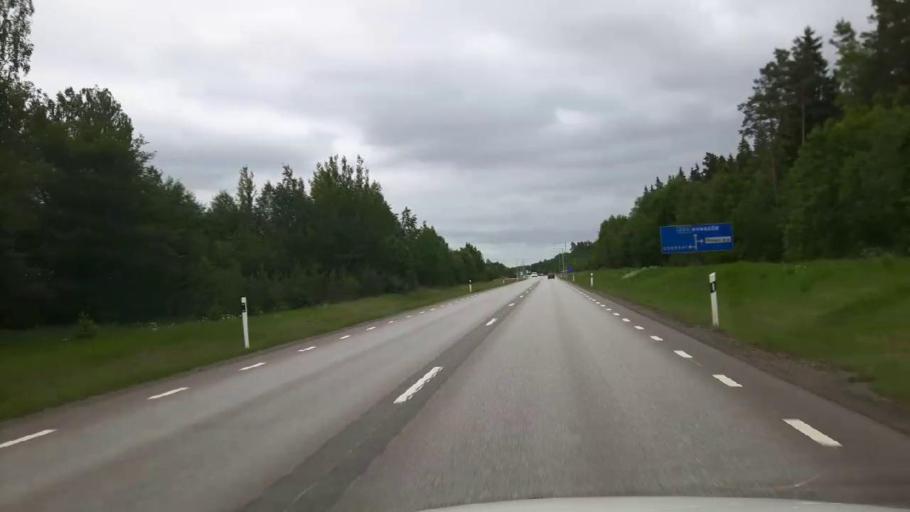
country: SE
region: Vaestmanland
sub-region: Kopings Kommun
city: Koping
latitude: 59.5461
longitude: 15.9255
